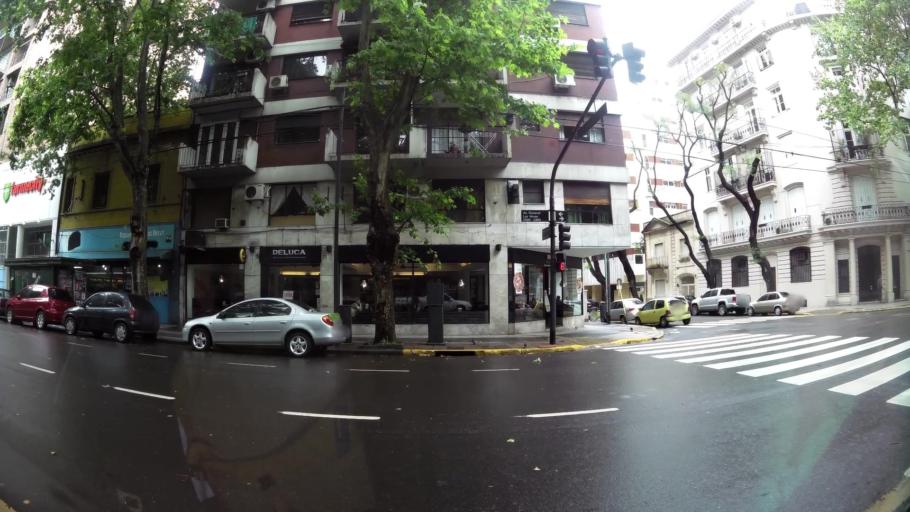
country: AR
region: Buenos Aires F.D.
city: Retiro
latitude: -34.5838
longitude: -58.4013
